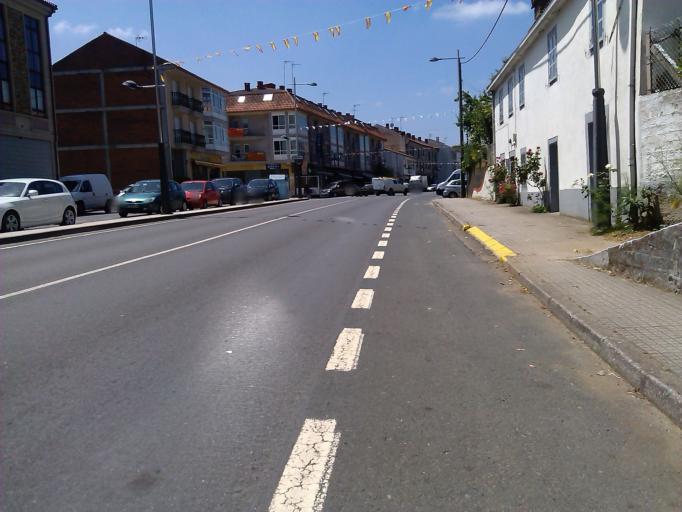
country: ES
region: Galicia
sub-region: Provincia da Coruna
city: Touro
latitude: 42.9064
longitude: -8.3601
